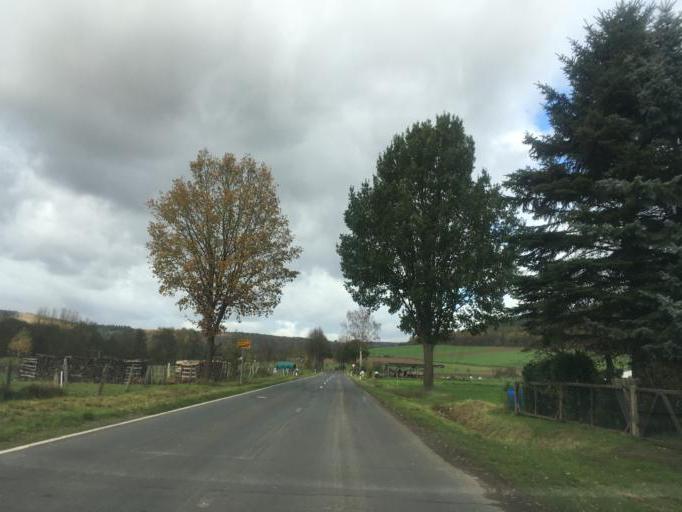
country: DE
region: Lower Saxony
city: Bodenfelde
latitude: 51.6325
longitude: 9.5227
